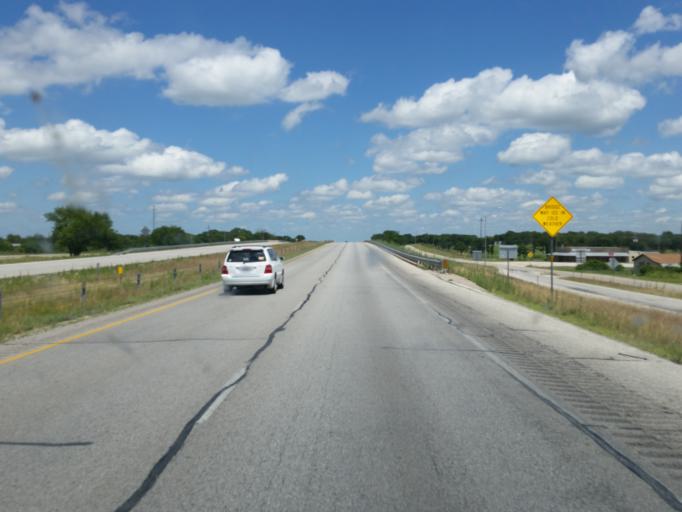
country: US
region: Texas
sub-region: Callahan County
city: Clyde
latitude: 32.4079
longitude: -99.4579
